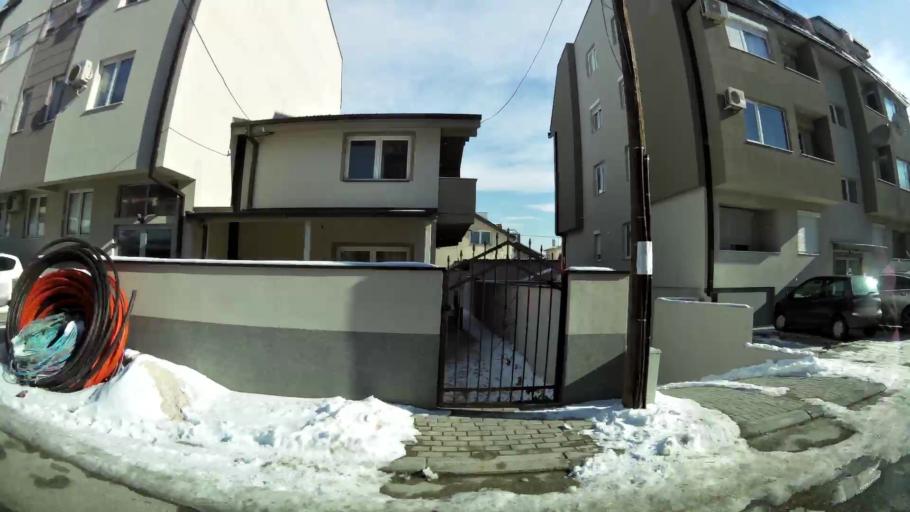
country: MK
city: Krushopek
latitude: 42.0014
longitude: 21.3698
